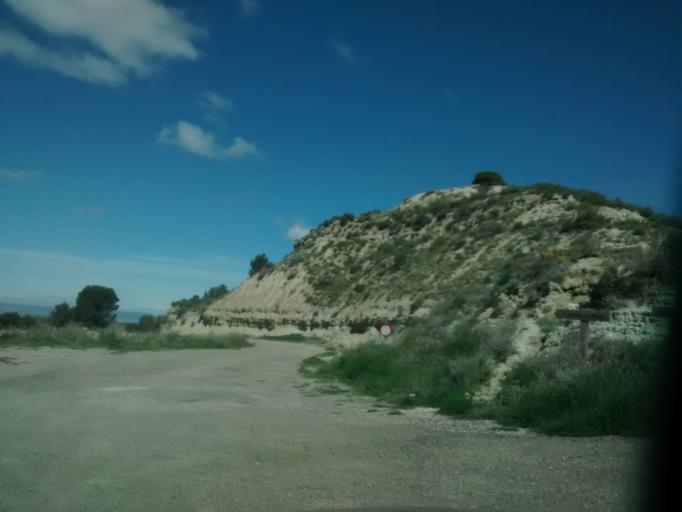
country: ES
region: Aragon
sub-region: Provincia de Huesca
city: Alcubierre
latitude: 41.8252
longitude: -0.5188
